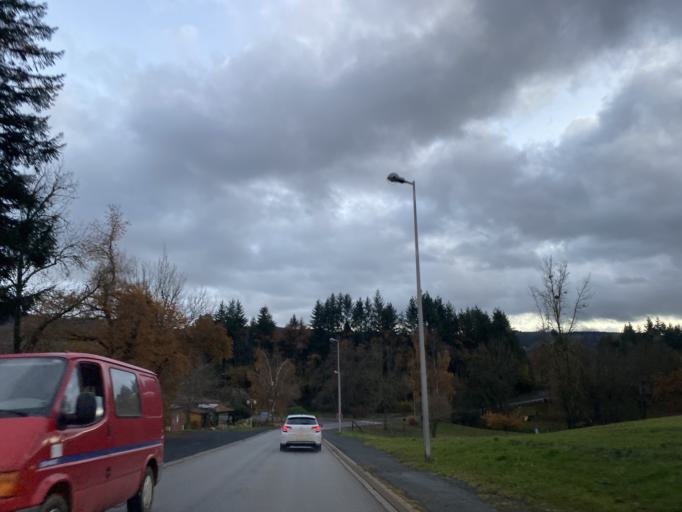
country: FR
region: Auvergne
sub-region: Departement du Puy-de-Dome
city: Cunlhat
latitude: 45.6258
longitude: 3.5624
